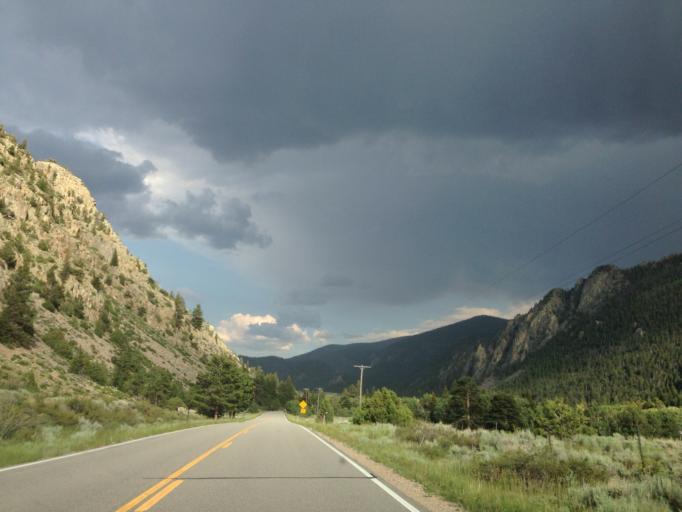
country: US
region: Colorado
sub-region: Larimer County
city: Estes Park
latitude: 40.7021
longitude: -105.7098
